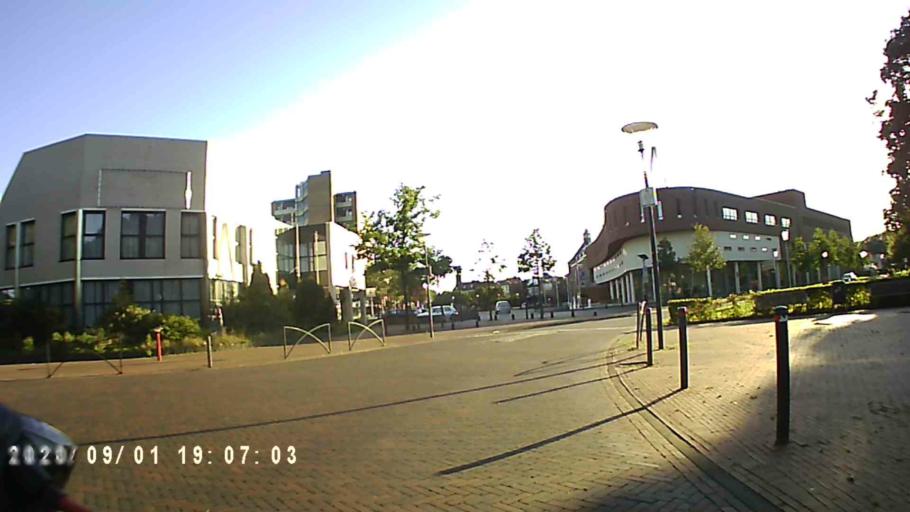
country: NL
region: Groningen
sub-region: Gemeente Veendam
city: Veendam
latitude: 53.1079
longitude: 6.8777
